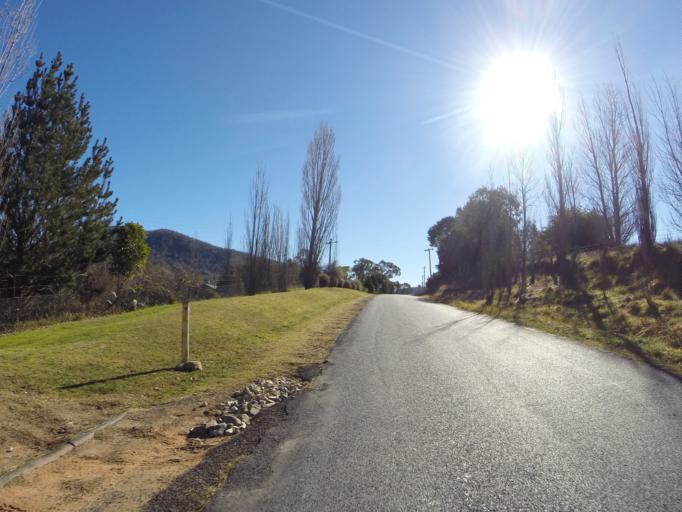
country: AU
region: New South Wales
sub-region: Oberon
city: Oberon
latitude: -33.5291
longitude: 149.9039
